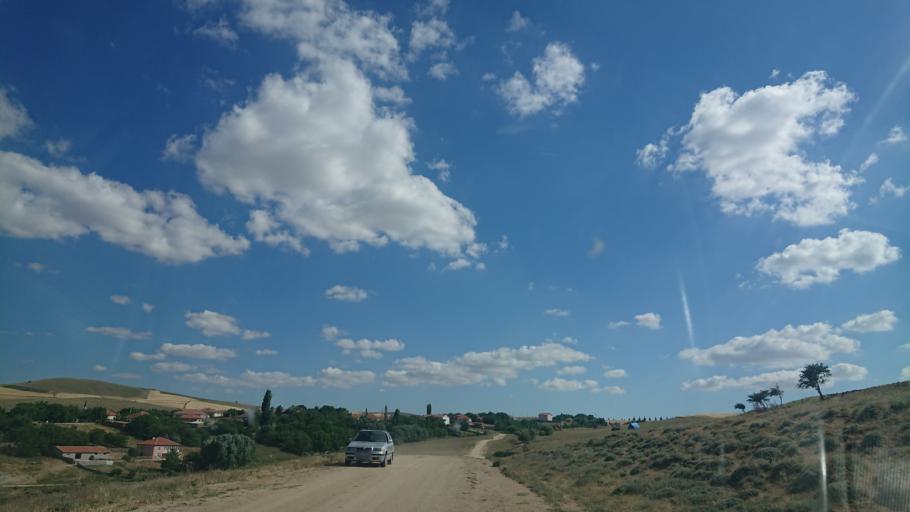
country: TR
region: Aksaray
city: Agacoren
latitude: 38.9091
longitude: 33.8567
